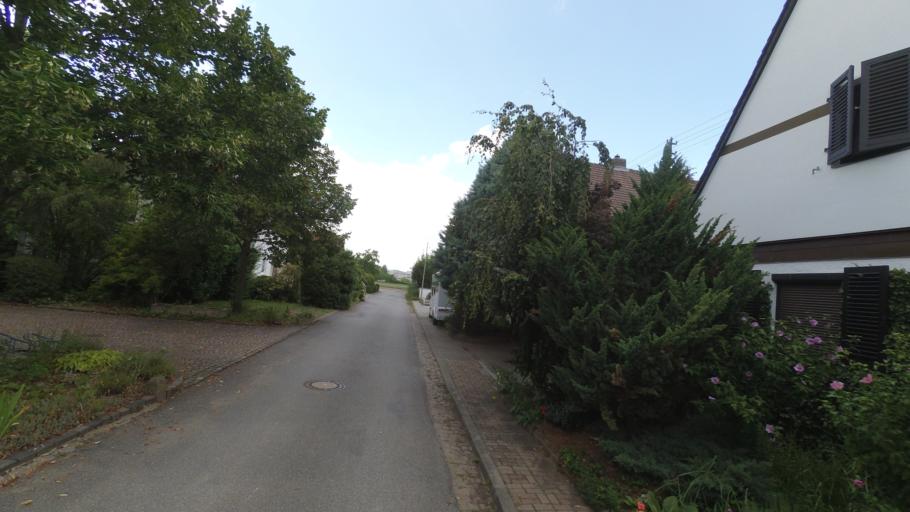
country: DE
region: Rheinland-Pfalz
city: Limburgerhof
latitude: 49.4069
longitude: 8.4029
